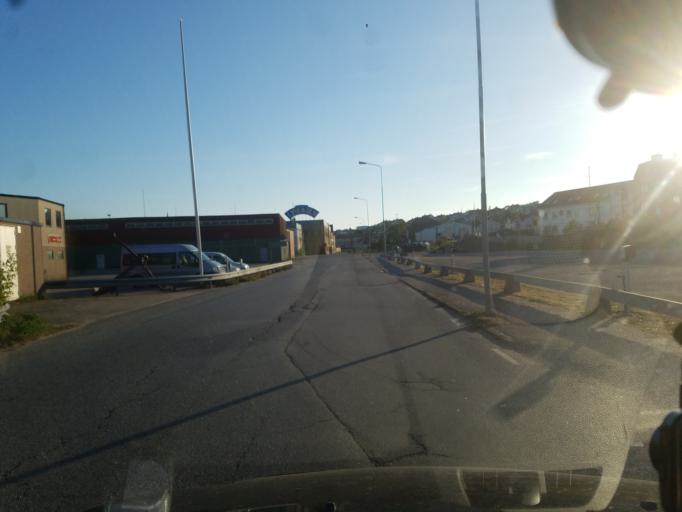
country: SE
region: Vaestra Goetaland
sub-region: Lysekils Kommun
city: Lysekil
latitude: 58.2767
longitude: 11.4480
